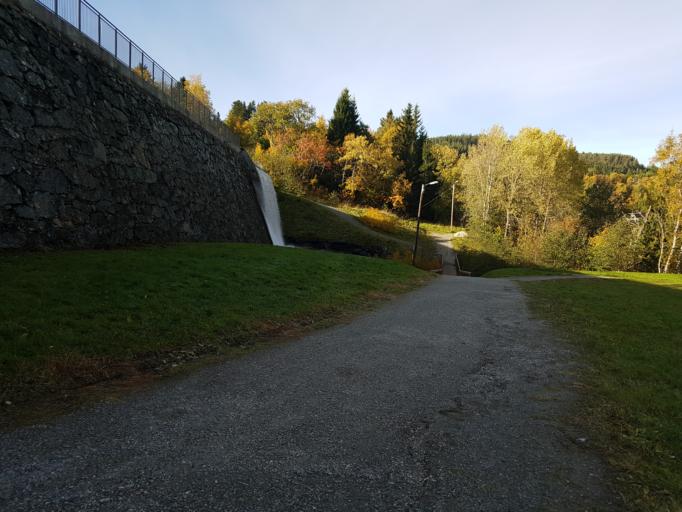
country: NO
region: Sor-Trondelag
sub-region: Trondheim
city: Trondheim
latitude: 63.4233
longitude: 10.3488
